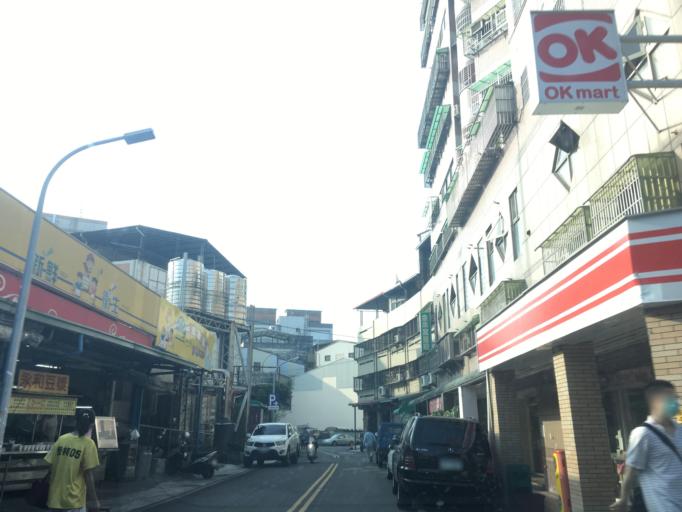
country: TW
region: Taiwan
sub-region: Taichung City
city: Taichung
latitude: 24.1701
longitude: 120.6904
